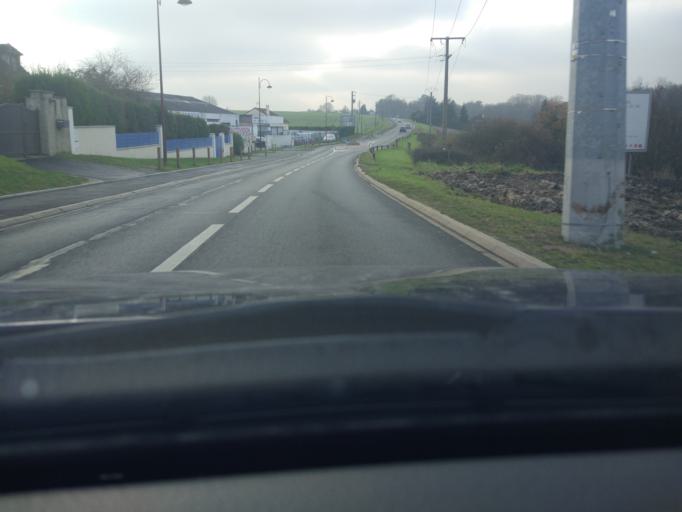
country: FR
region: Ile-de-France
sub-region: Departement de l'Essonne
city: Egly
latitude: 48.5796
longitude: 2.2142
